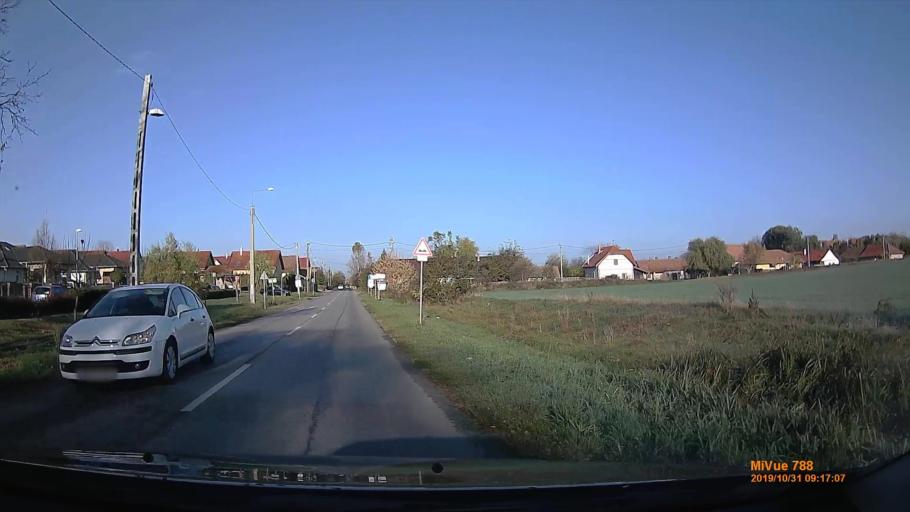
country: HU
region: Pest
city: Peteri
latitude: 47.4066
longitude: 19.4086
